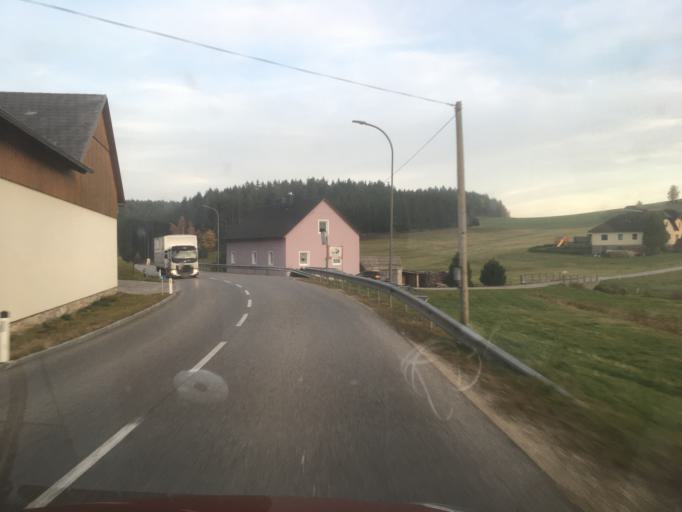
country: AT
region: Lower Austria
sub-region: Politischer Bezirk Zwettl
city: Langschlag
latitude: 48.5783
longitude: 14.8565
